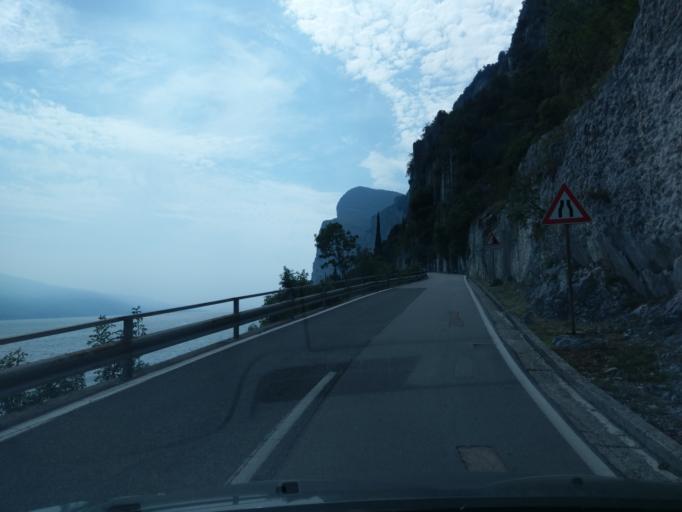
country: IT
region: Lombardy
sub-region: Provincia di Brescia
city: Pieve
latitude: 45.7681
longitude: 10.7616
